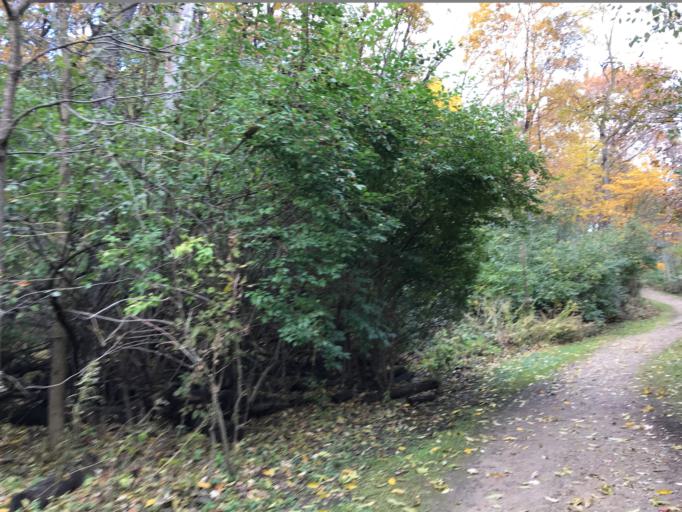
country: US
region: Michigan
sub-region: Washtenaw County
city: Ann Arbor
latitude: 42.2566
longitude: -83.7072
